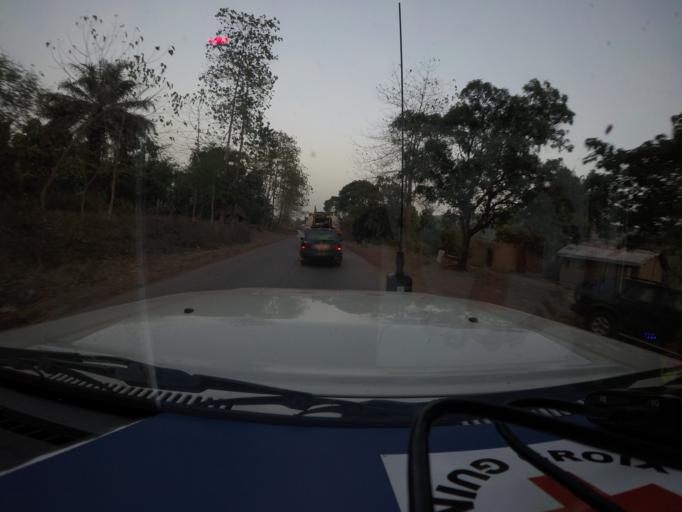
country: GN
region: Kindia
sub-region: Kindia
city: Kindia
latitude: 9.9023
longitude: -13.0047
